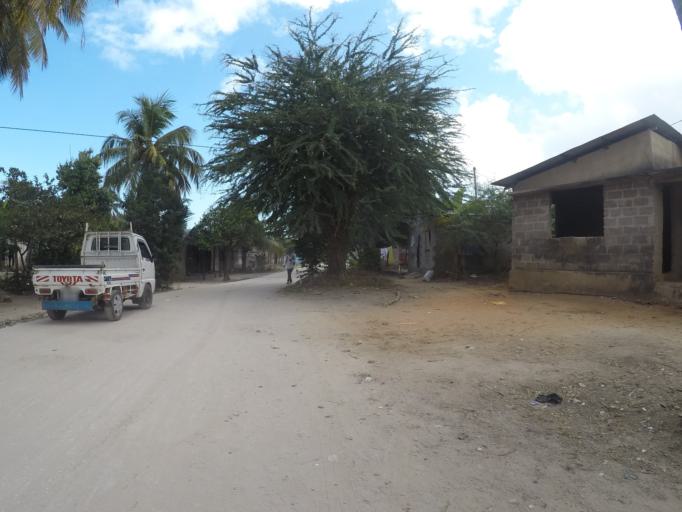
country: TZ
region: Zanzibar Urban/West
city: Zanzibar
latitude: -6.1849
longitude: 39.2118
